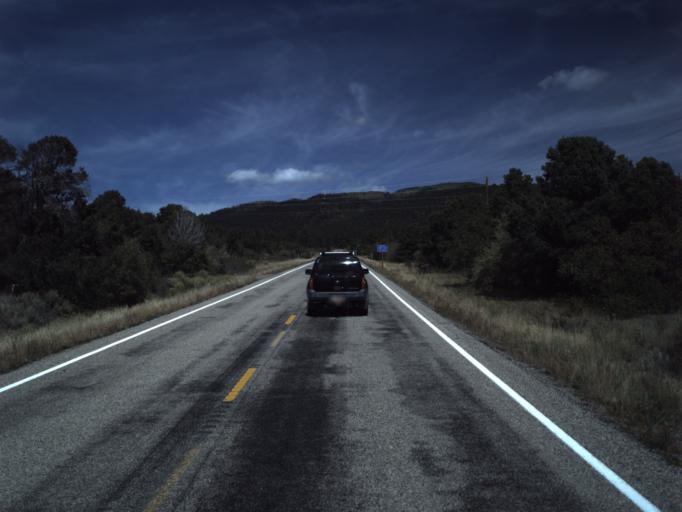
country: US
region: Utah
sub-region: Wayne County
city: Loa
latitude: 37.9777
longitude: -111.4309
